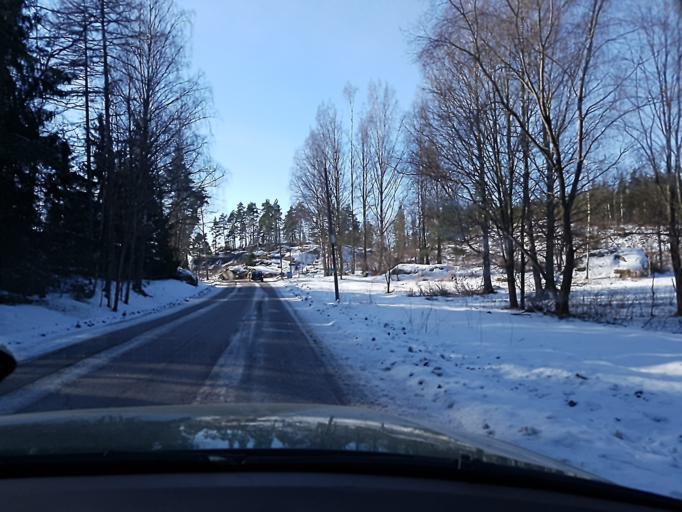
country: FI
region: Uusimaa
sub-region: Helsinki
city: Siuntio
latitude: 60.1148
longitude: 24.3025
